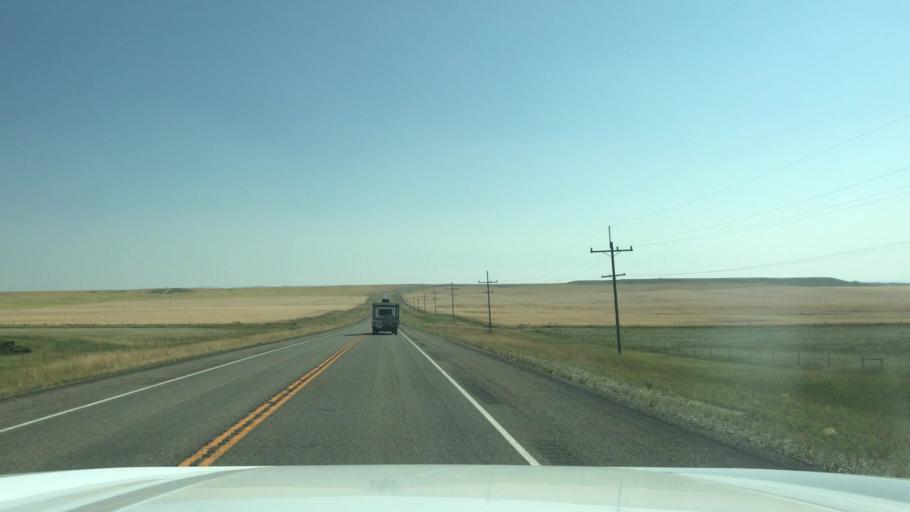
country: US
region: Montana
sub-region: Wheatland County
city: Harlowton
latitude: 46.4920
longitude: -109.7661
